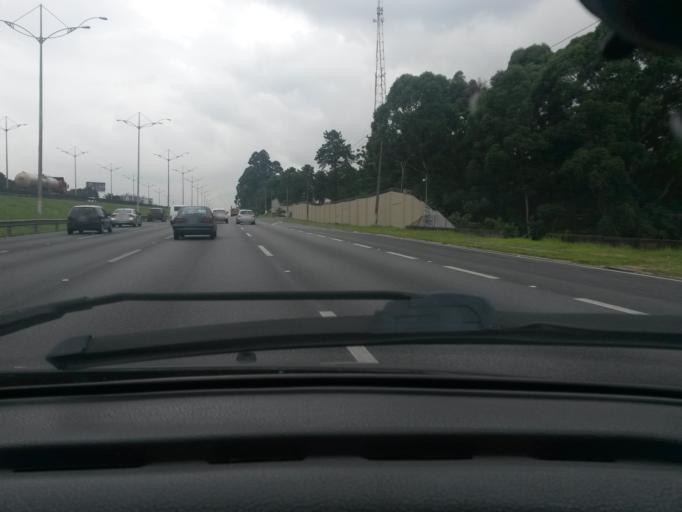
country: BR
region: Sao Paulo
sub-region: Sao Bernardo Do Campo
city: Sao Bernardo do Campo
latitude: -23.6763
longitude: -46.5698
